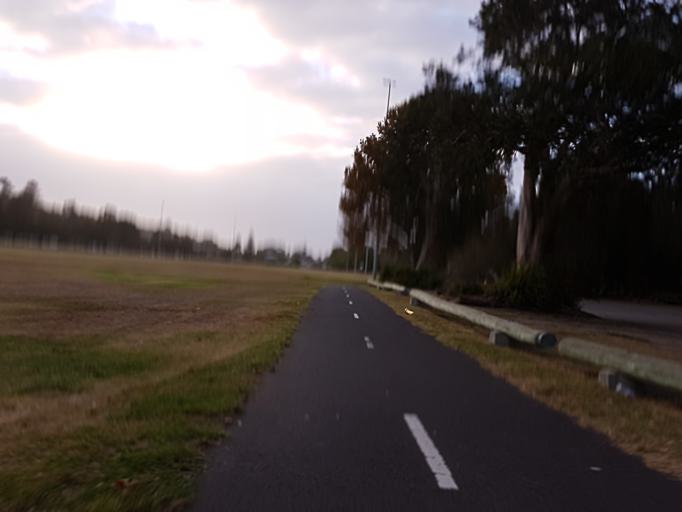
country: AU
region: New South Wales
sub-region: Warringah
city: North Manly
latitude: -33.7781
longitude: 151.2711
